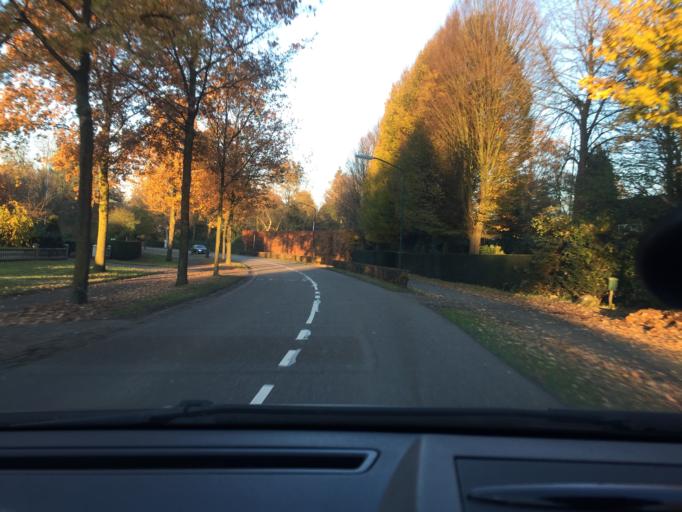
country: NL
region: North Brabant
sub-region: Gemeente Laarbeek
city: Aarle-Rixtel
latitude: 51.5060
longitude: 5.6501
